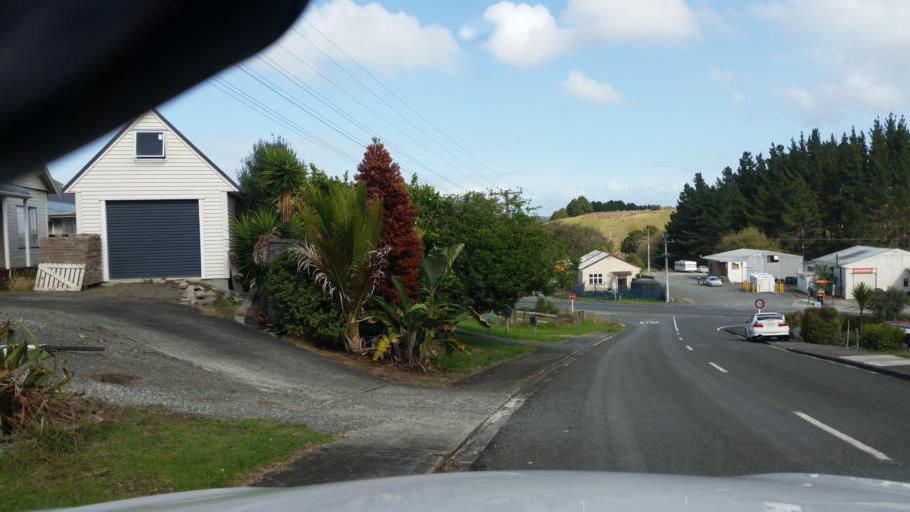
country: NZ
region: Northland
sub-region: Whangarei
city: Ruakaka
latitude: -36.1040
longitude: 174.3681
